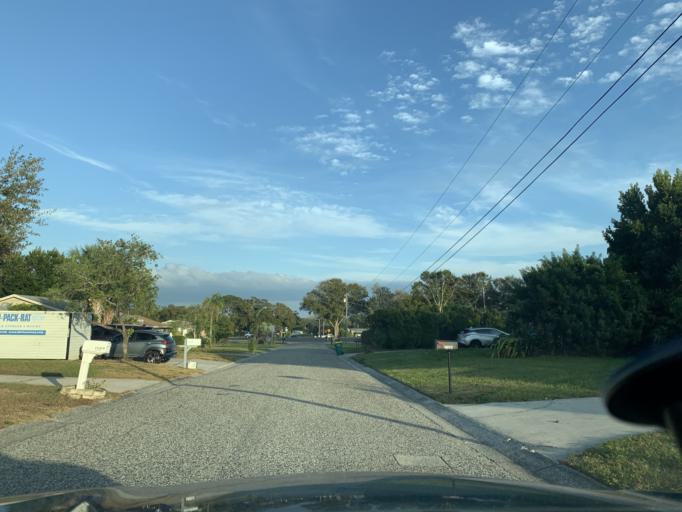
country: US
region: Florida
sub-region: Pinellas County
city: Ridgecrest
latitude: 27.8838
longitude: -82.7967
